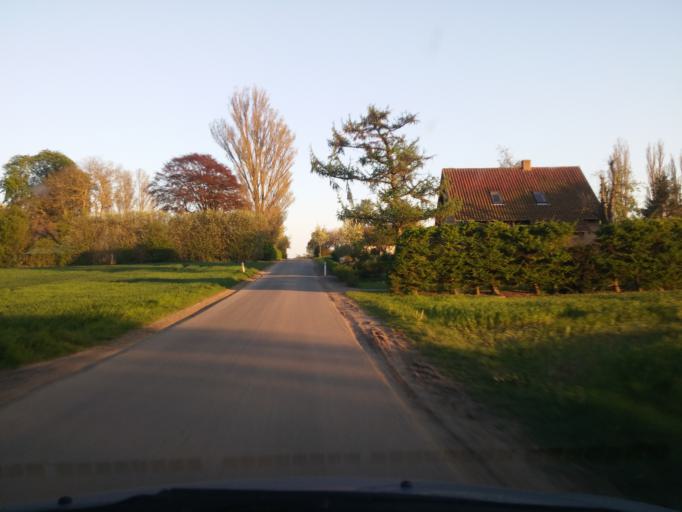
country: DK
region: South Denmark
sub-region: Nyborg Kommune
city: Ullerslev
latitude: 55.3869
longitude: 10.6389
